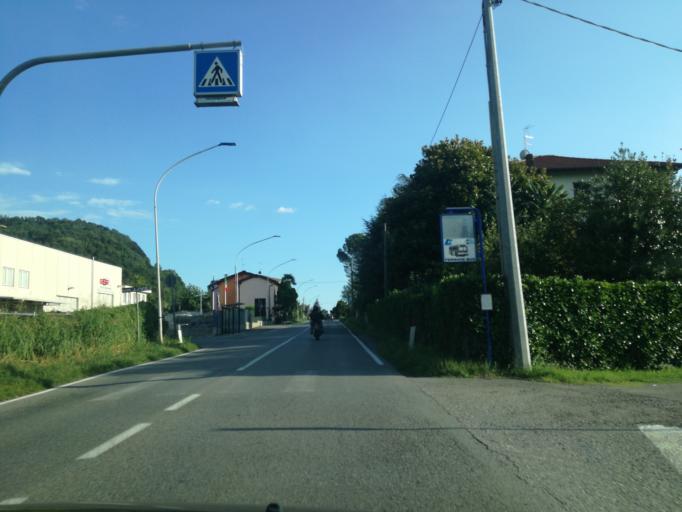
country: IT
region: Lombardy
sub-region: Provincia di Lecco
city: Calolziocorte
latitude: 45.7821
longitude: 9.4413
